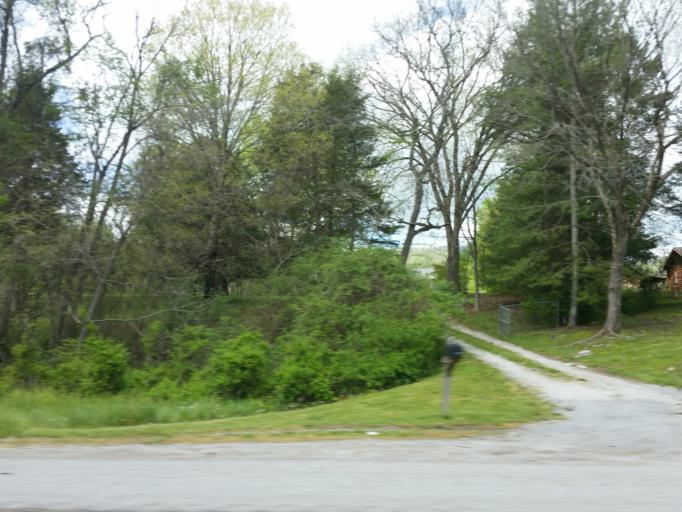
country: US
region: Kentucky
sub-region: Bell County
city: Middlesboro
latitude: 36.5293
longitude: -83.7232
